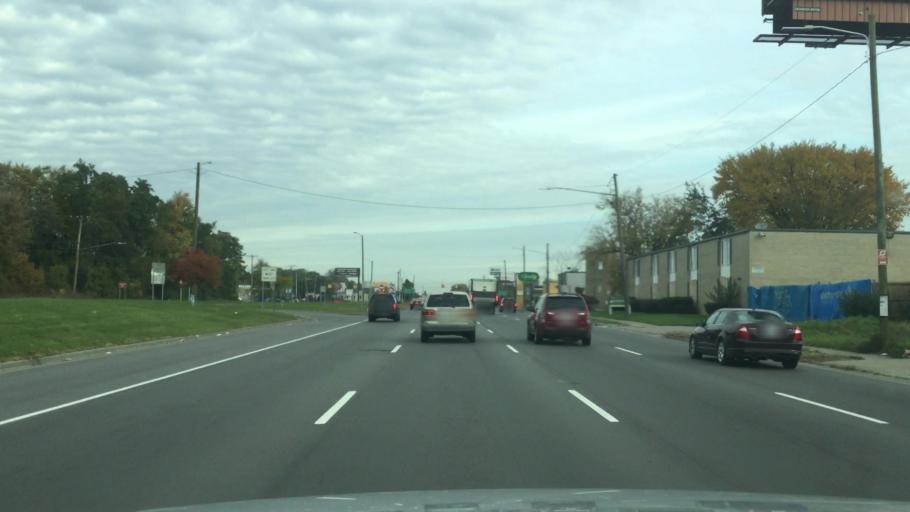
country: US
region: Michigan
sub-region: Wayne County
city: Redford
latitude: 42.4117
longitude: -83.2769
